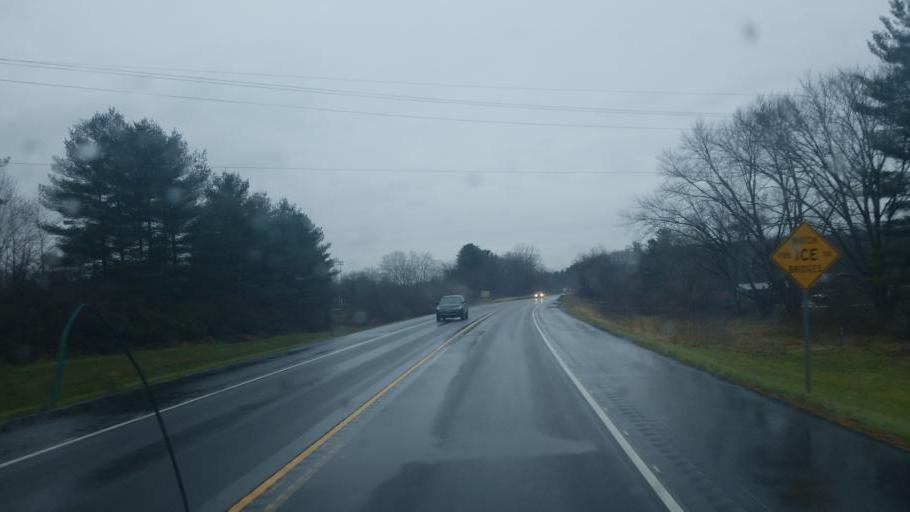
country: US
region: Indiana
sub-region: Brown County
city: Nashville
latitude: 39.1980
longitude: -86.2204
